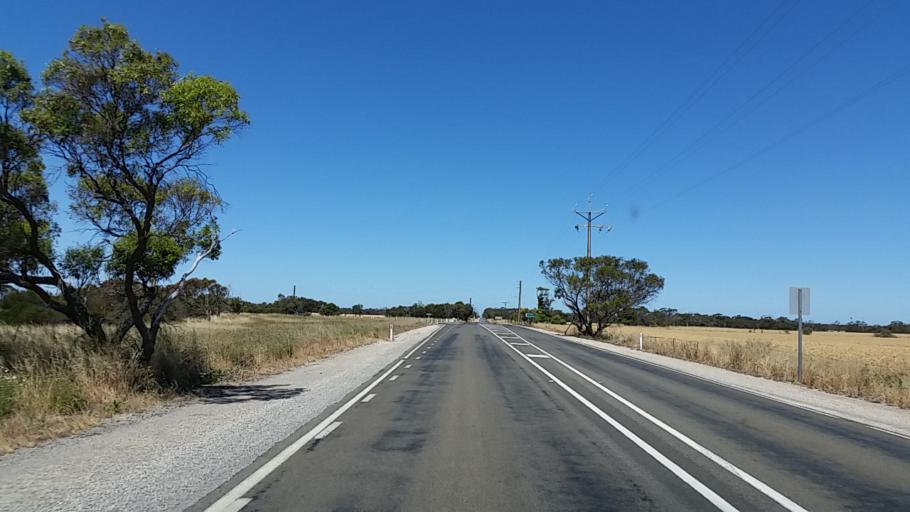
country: AU
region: South Australia
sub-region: Yorke Peninsula
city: Honiton
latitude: -35.0134
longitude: 137.6612
